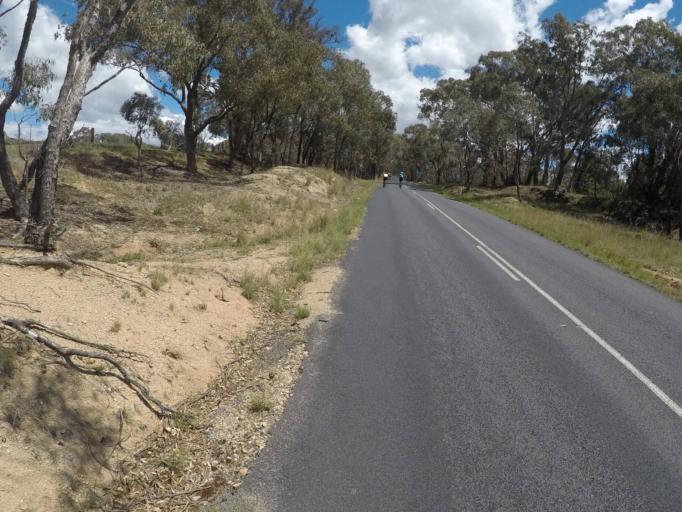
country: AU
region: New South Wales
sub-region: Blayney
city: Blayney
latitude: -33.5801
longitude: 149.3969
